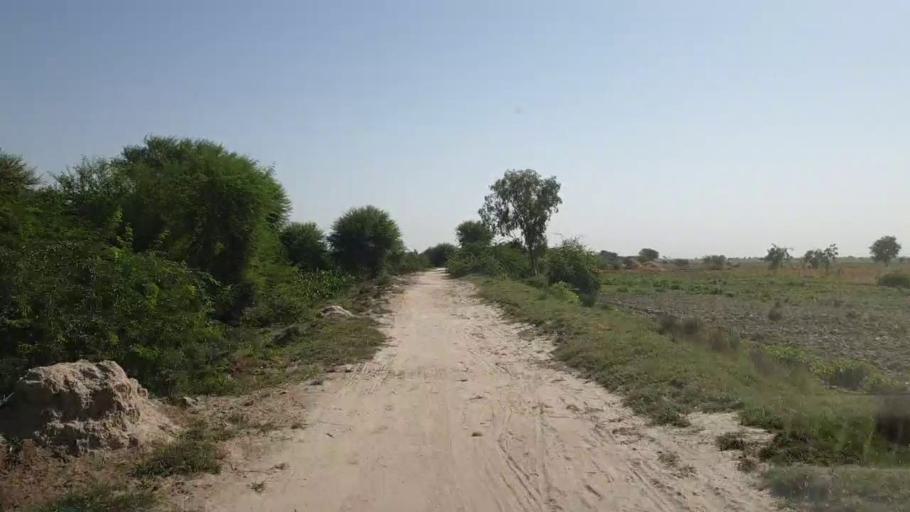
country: PK
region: Sindh
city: Kadhan
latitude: 24.6322
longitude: 68.9926
